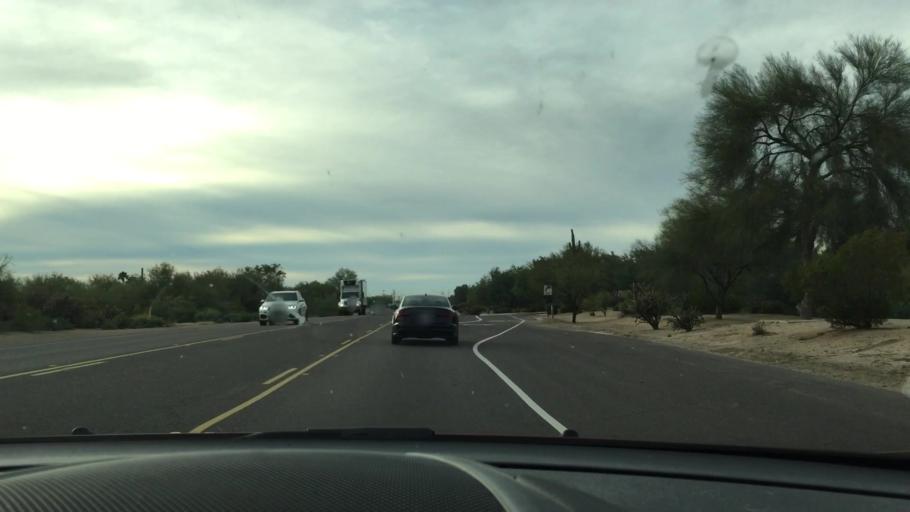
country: US
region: Arizona
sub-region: Maricopa County
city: Carefree
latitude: 33.6987
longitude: -111.9106
